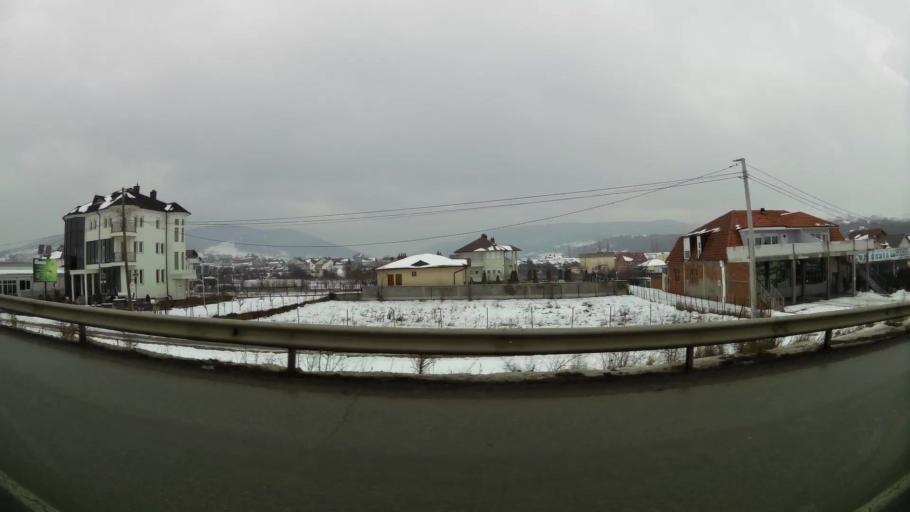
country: XK
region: Pristina
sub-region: Komuna e Prishtines
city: Pristina
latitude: 42.7096
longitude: 21.1530
